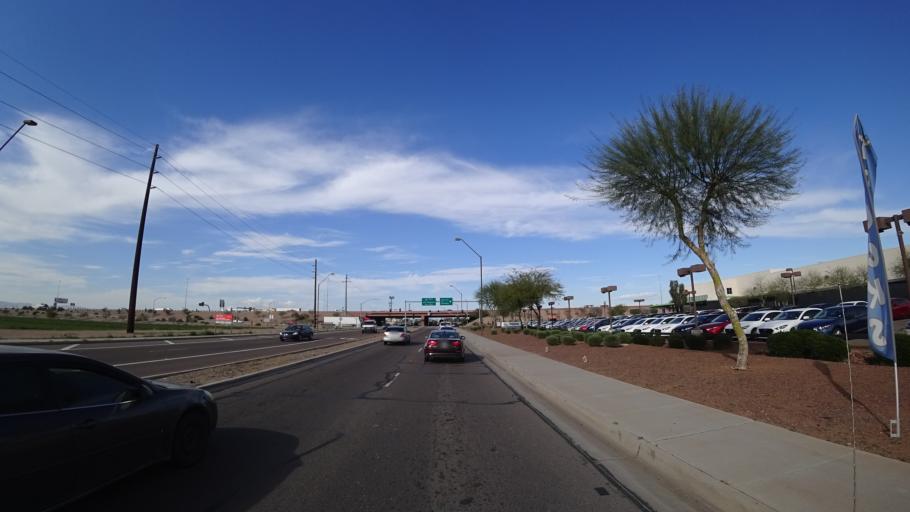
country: US
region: Arizona
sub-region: Maricopa County
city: Tolleson
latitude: 33.4593
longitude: -112.2898
